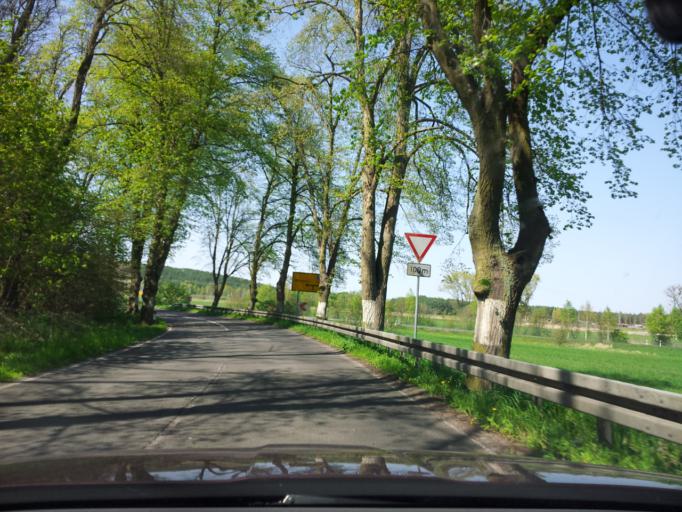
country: DE
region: Brandenburg
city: Michendorf
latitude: 52.3176
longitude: 13.1136
